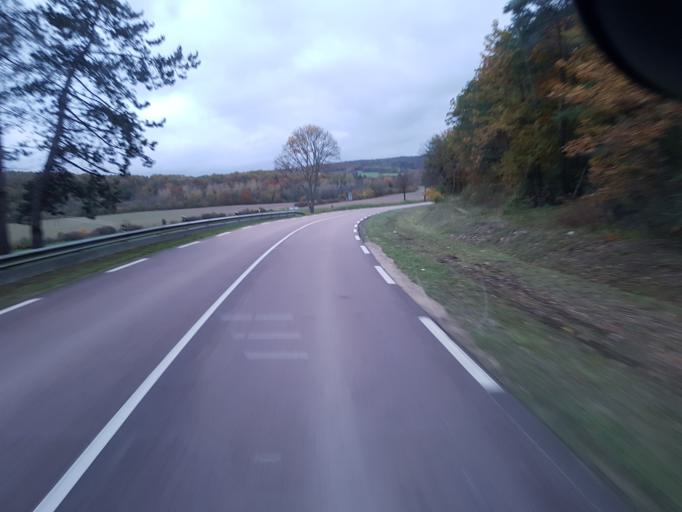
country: FR
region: Champagne-Ardenne
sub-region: Departement de l'Aube
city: Mussy-sur-Seine
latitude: 48.0012
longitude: 4.4748
